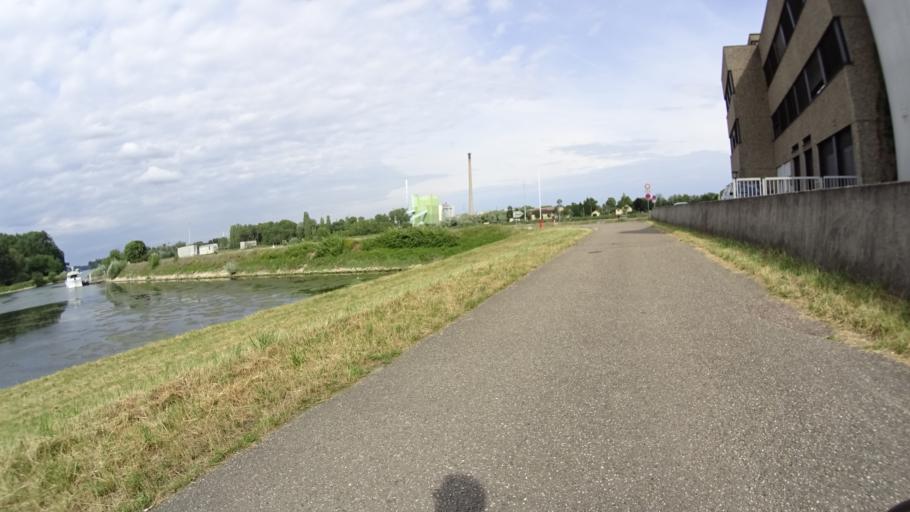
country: DE
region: Rheinland-Pfalz
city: Worth am Rhein
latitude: 49.0396
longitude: 8.3014
